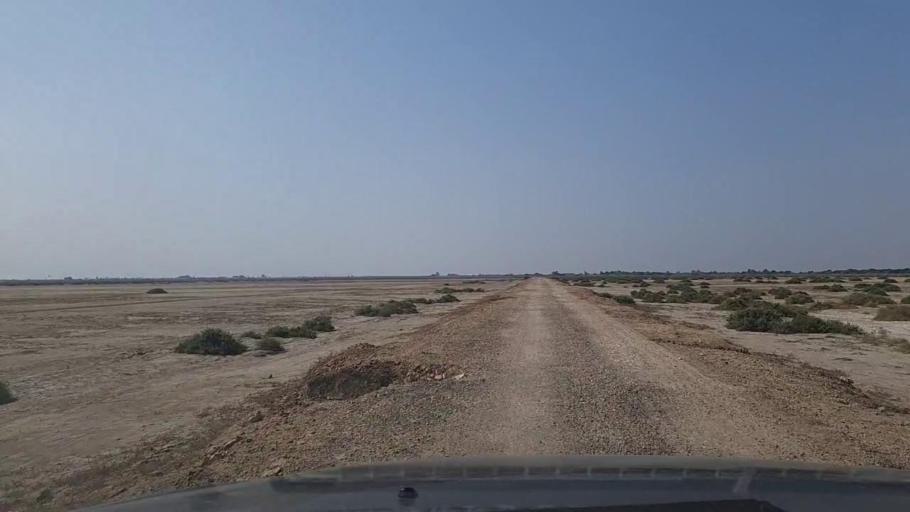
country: PK
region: Sindh
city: Mirpur Sakro
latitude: 24.4324
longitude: 67.7314
